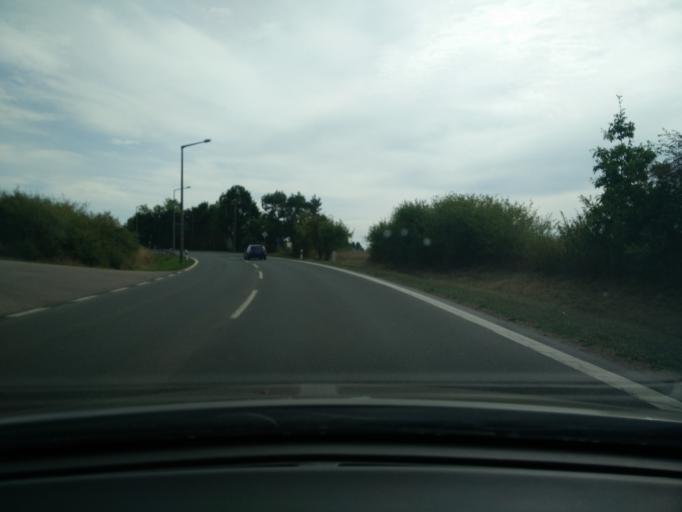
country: DE
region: Bavaria
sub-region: Regierungsbezirk Mittelfranken
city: Zirndorf
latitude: 49.4838
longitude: 10.9322
